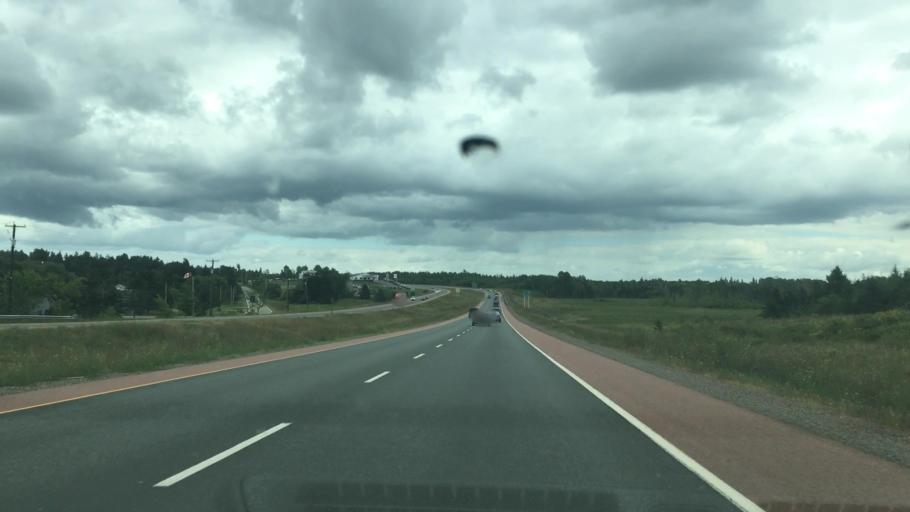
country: CA
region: Nova Scotia
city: Antigonish
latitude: 45.5969
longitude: -62.0413
